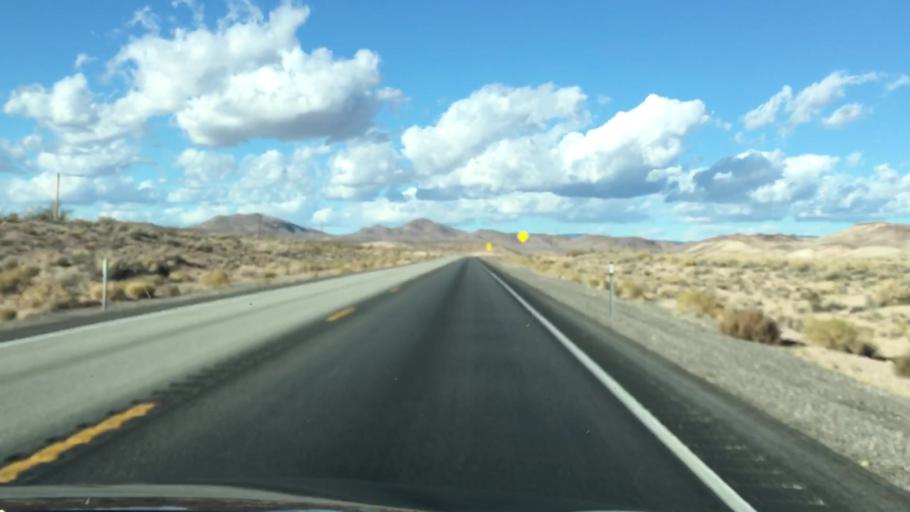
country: US
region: Nevada
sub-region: Nye County
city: Beatty
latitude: 36.9855
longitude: -116.7247
